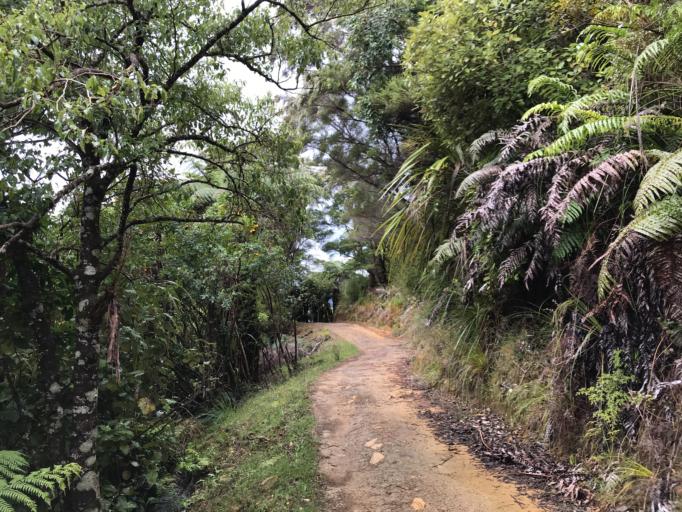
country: NZ
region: Marlborough
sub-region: Marlborough District
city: Picton
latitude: -41.1145
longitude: 174.1636
